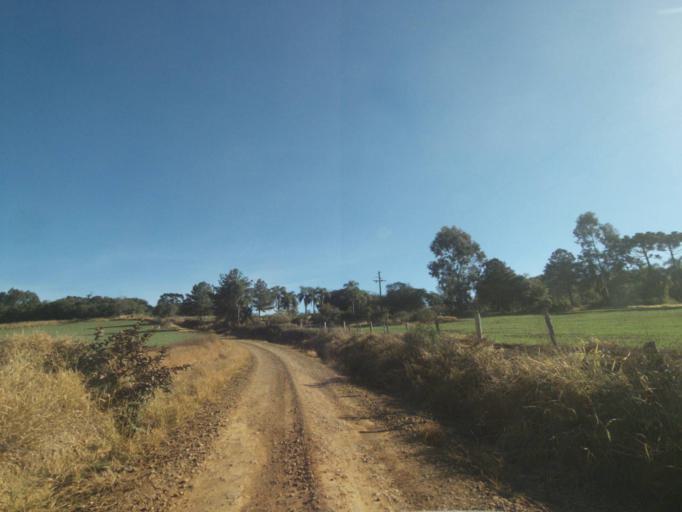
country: BR
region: Parana
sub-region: Tibagi
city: Tibagi
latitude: -24.5516
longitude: -50.5198
